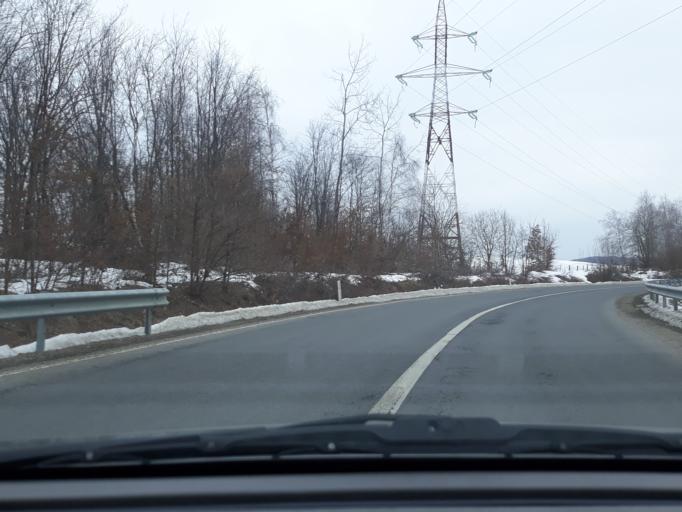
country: RO
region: Bihor
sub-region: Oras Alesd
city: Padurea Neagra
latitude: 47.1213
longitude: 22.4310
